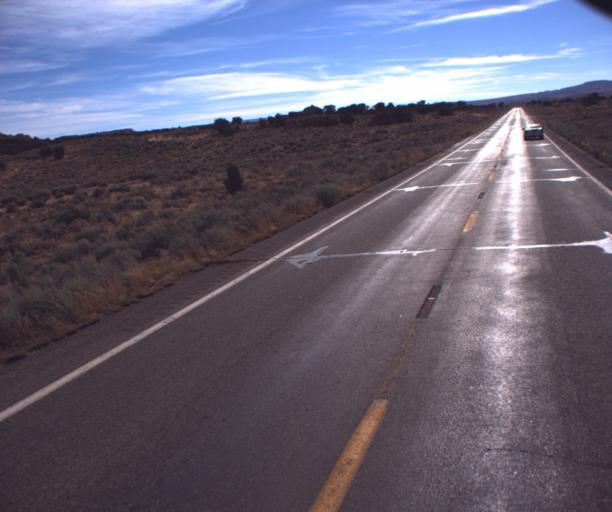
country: US
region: Arizona
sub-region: Coconino County
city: Kaibito
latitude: 36.6354
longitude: -111.2124
